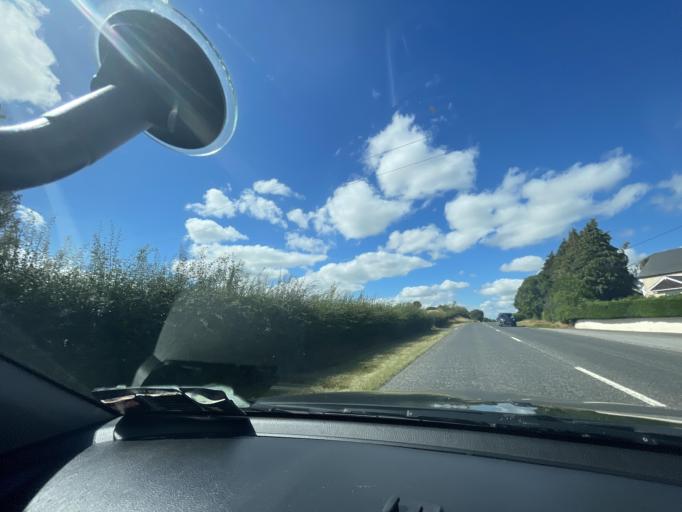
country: IE
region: Leinster
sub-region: An Mhi
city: Newtown Trim
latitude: 53.5297
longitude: -6.6869
